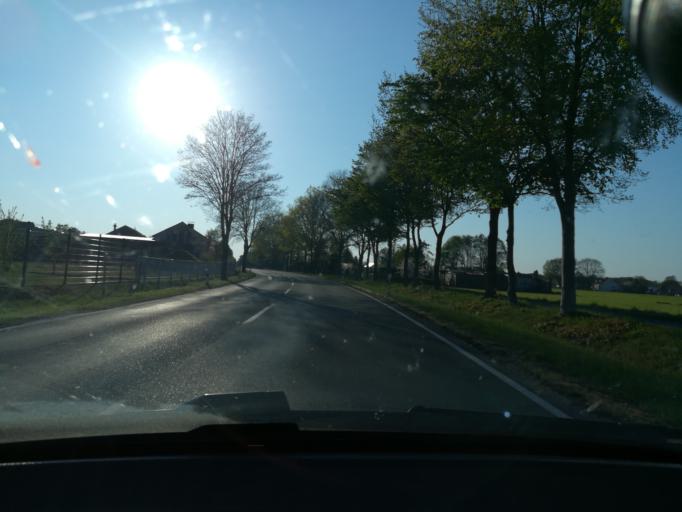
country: DE
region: North Rhine-Westphalia
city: Versmold
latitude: 52.0421
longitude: 8.1675
